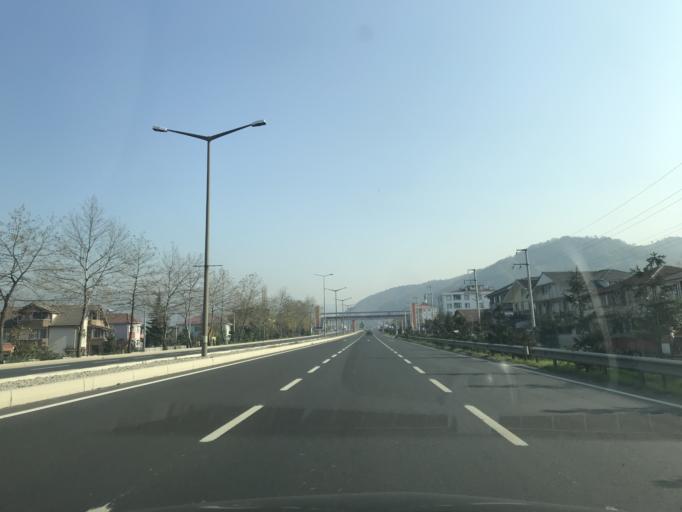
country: TR
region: Duzce
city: Kaynasli
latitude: 40.7746
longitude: 31.3126
